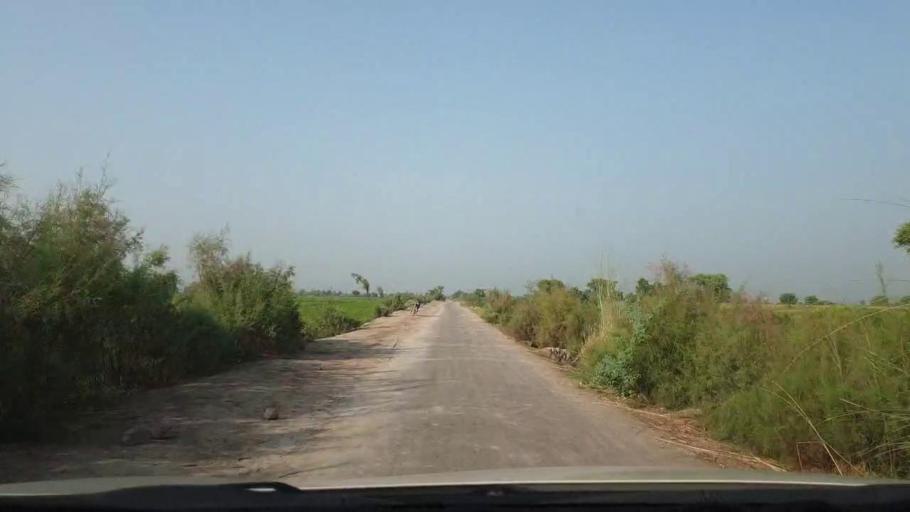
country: PK
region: Sindh
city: Larkana
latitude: 27.4999
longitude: 68.1746
